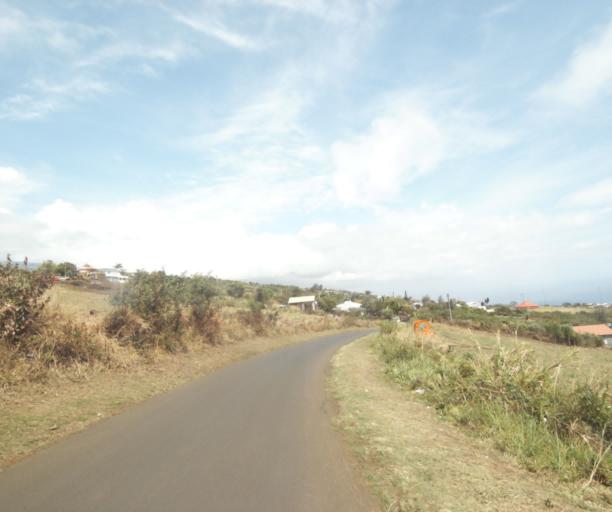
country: RE
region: Reunion
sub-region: Reunion
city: Trois-Bassins
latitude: -21.0942
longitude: 55.2762
